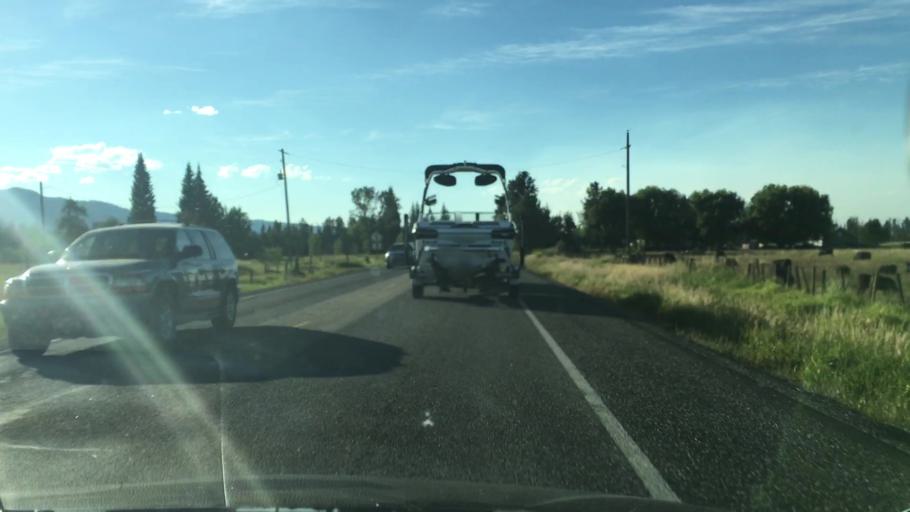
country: US
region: Idaho
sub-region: Valley County
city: McCall
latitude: 44.7231
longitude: -116.0701
